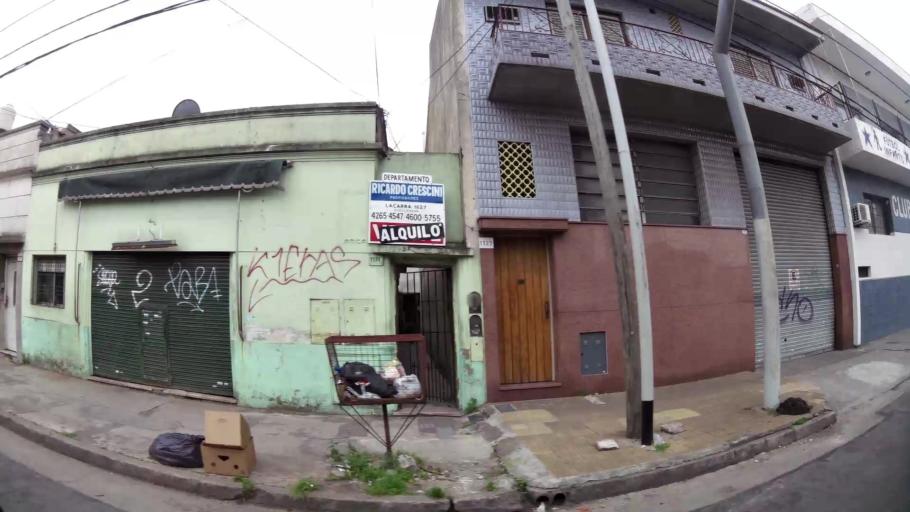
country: AR
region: Buenos Aires
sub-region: Partido de Avellaneda
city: Avellaneda
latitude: -34.6805
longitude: -58.3688
